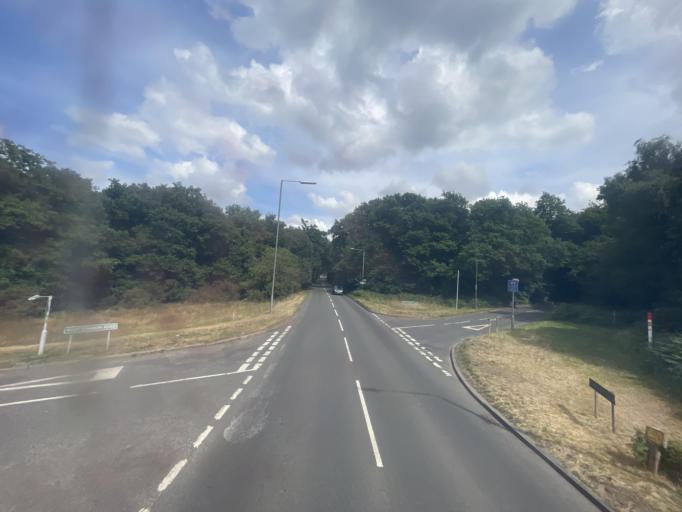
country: GB
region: England
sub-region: Greater London
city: West Wickham
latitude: 51.3673
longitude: 0.0202
